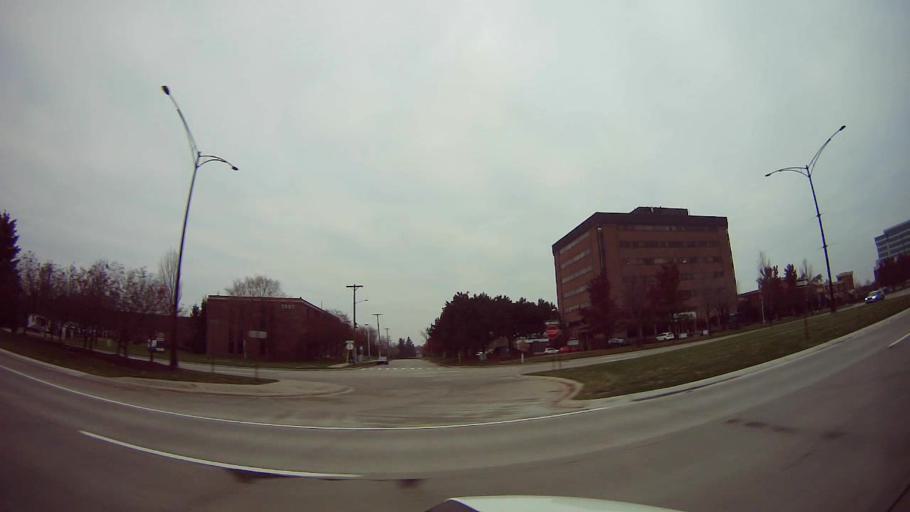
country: US
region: Michigan
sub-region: Oakland County
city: Clawson
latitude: 42.5618
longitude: -83.1743
